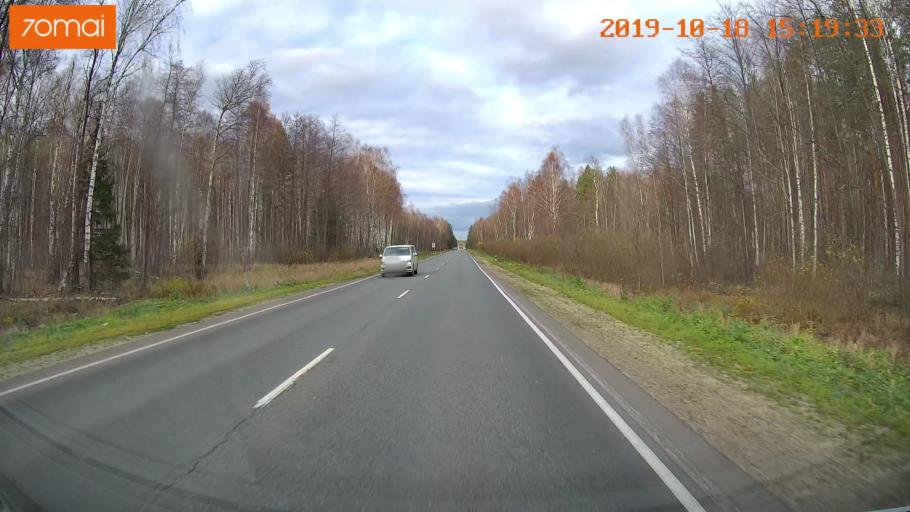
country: RU
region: Vladimir
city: Anopino
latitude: 55.6746
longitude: 40.7385
